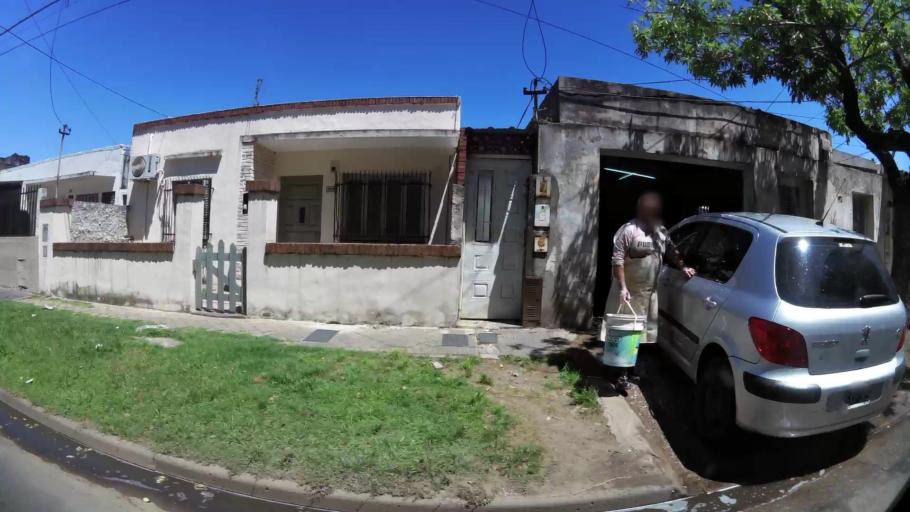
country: AR
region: Santa Fe
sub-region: Departamento de Rosario
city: Rosario
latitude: -32.9428
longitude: -60.7113
